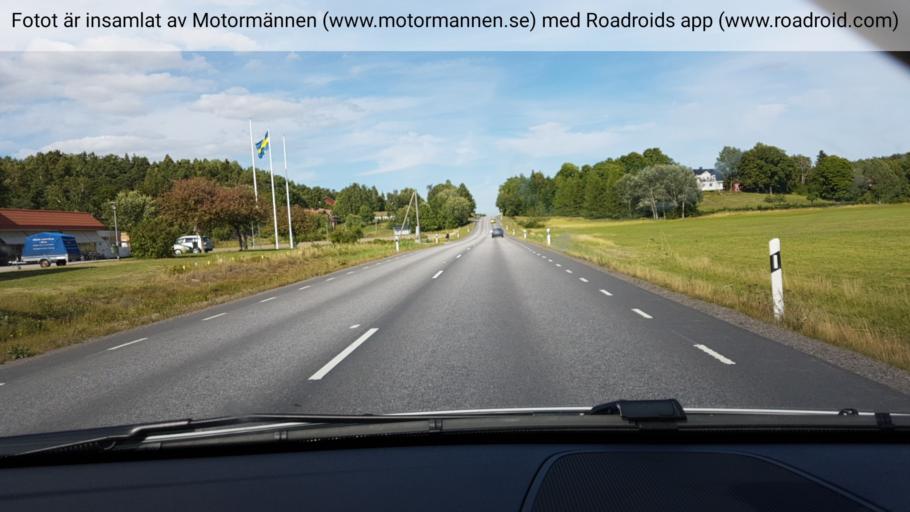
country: SE
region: Stockholm
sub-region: Sodertalje Kommun
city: Pershagen
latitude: 59.0859
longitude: 17.6097
